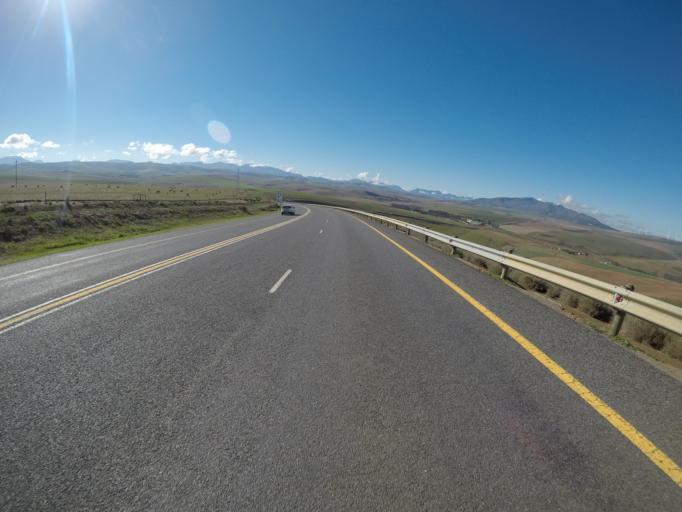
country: ZA
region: Western Cape
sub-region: Overberg District Municipality
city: Caledon
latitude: -34.2160
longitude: 19.3189
